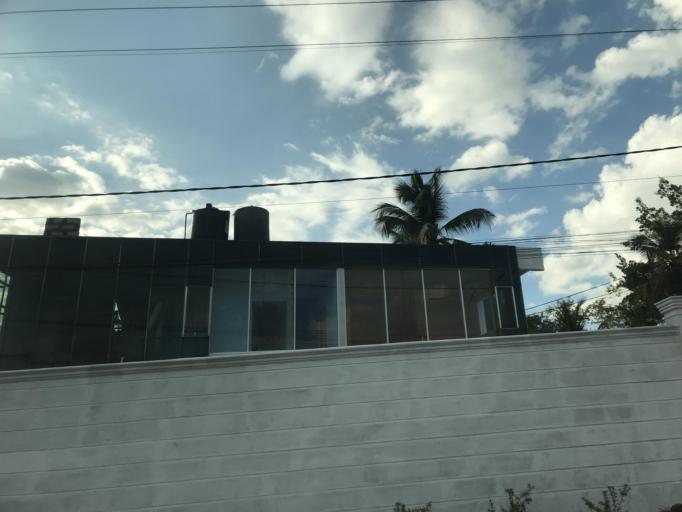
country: LK
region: Western
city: Gampaha
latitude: 7.0589
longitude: 80.0088
